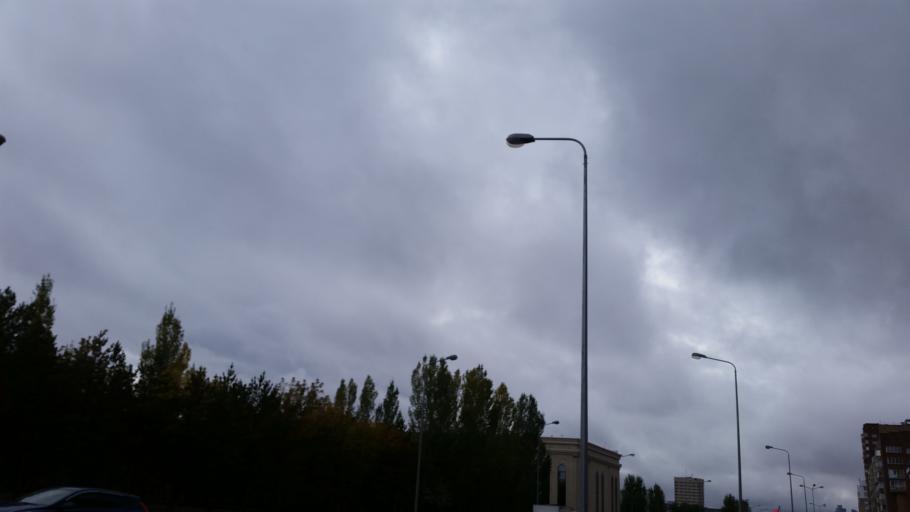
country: KZ
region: Astana Qalasy
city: Astana
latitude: 51.1484
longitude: 71.4861
